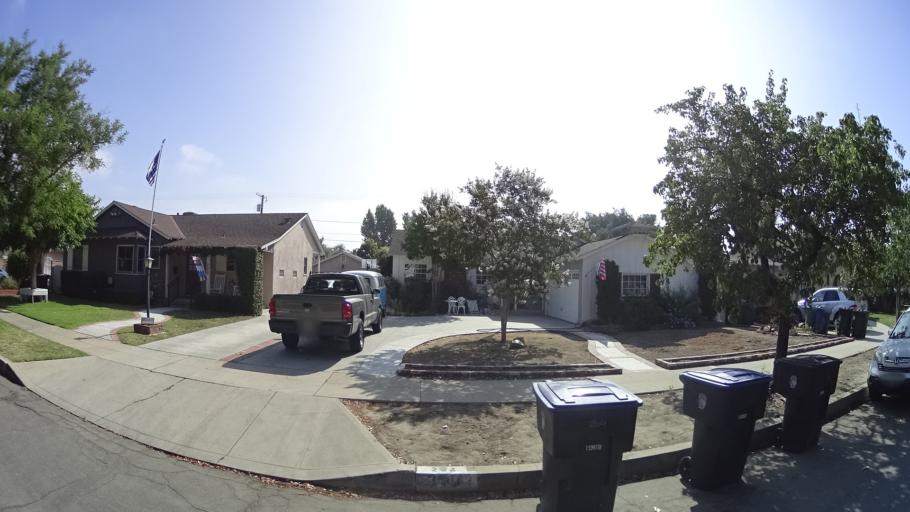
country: US
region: California
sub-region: Los Angeles County
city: Burbank
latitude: 34.1657
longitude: -118.3234
